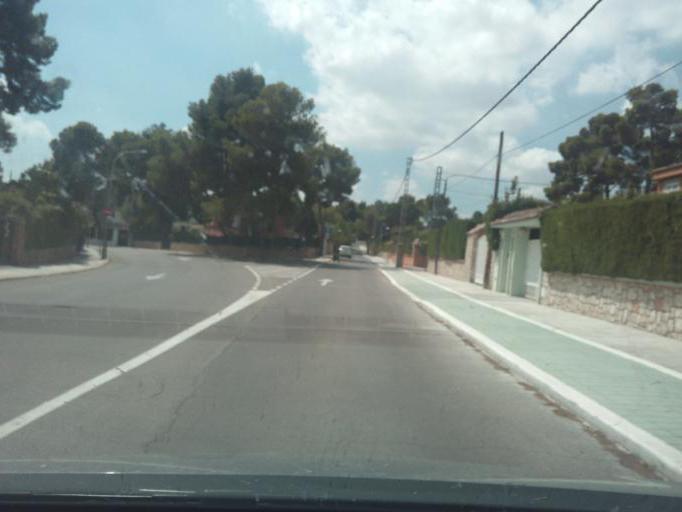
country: ES
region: Valencia
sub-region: Provincia de Valencia
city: Manises
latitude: 39.5342
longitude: -0.4851
